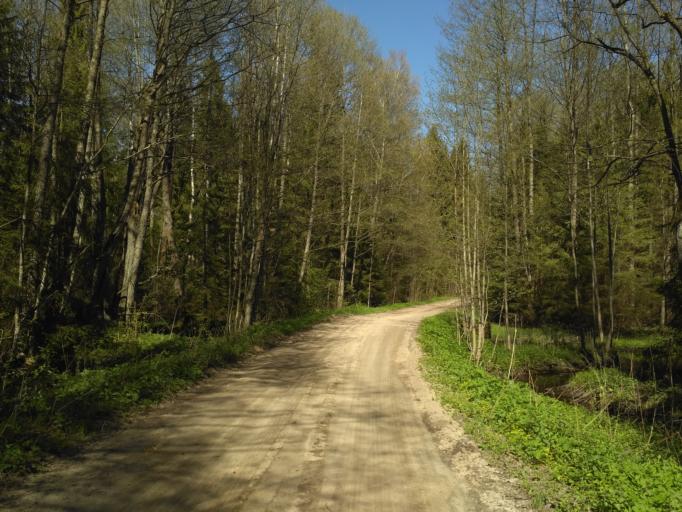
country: BY
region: Minsk
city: Horad Barysaw
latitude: 54.5211
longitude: 28.5253
